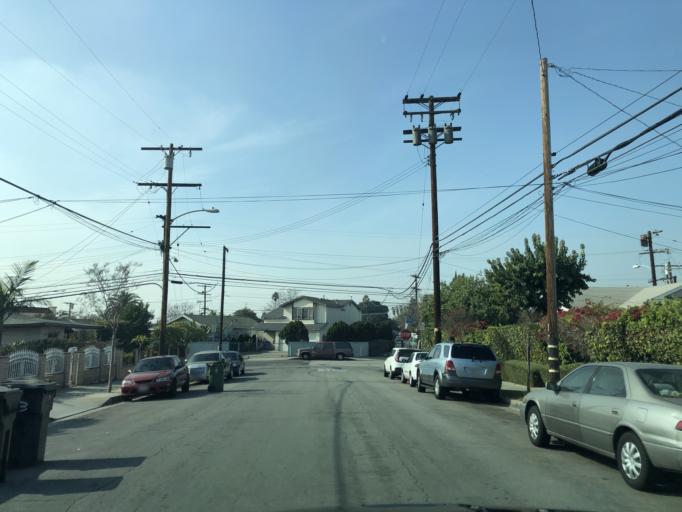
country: US
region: California
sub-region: Los Angeles County
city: Boyle Heights
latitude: 34.0381
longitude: -118.1919
